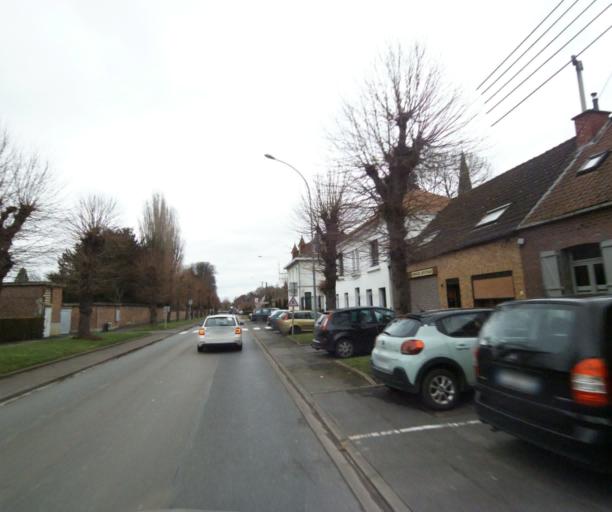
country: FR
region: Nord-Pas-de-Calais
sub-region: Departement du Nord
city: Saint-Saulve
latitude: 50.3712
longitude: 3.5484
